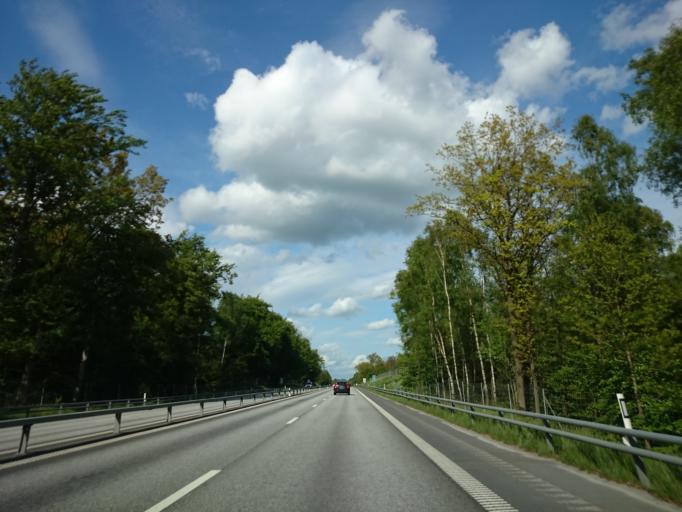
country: SE
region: Skane
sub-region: Horby Kommun
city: Hoerby
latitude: 55.9170
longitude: 13.7790
